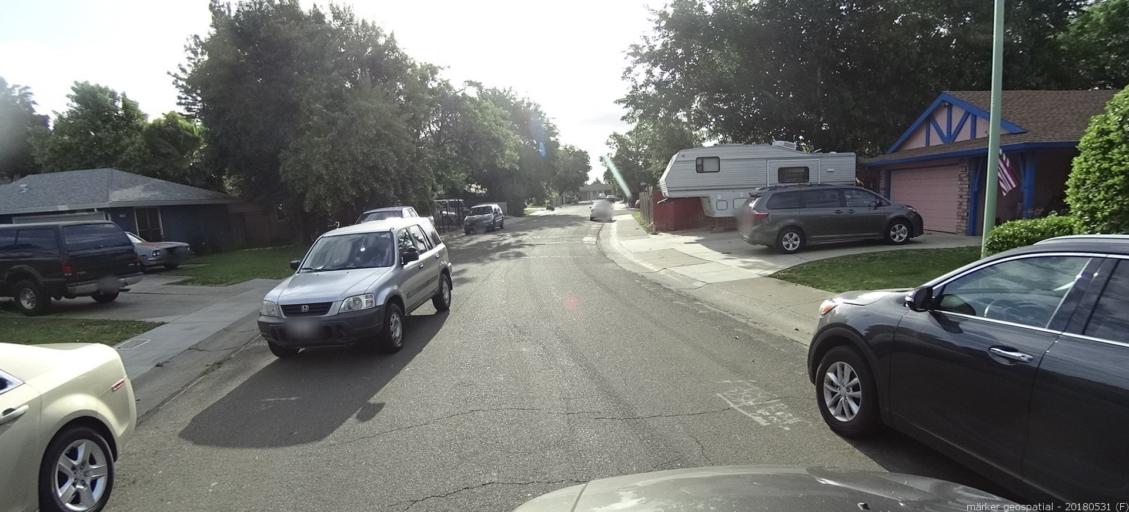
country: US
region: California
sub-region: Sacramento County
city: Sacramento
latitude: 38.6261
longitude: -121.4868
